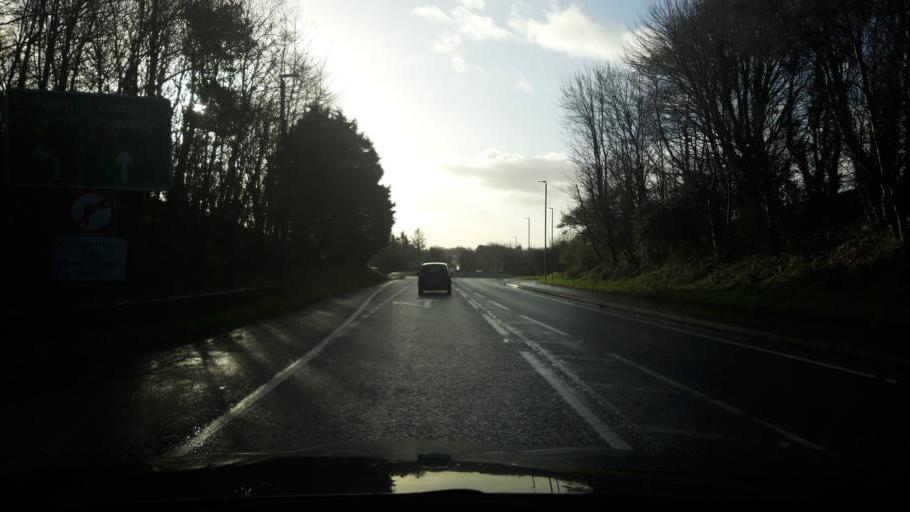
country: GB
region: Northern Ireland
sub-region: Coleraine District
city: Coleraine
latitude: 55.1089
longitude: -6.6928
